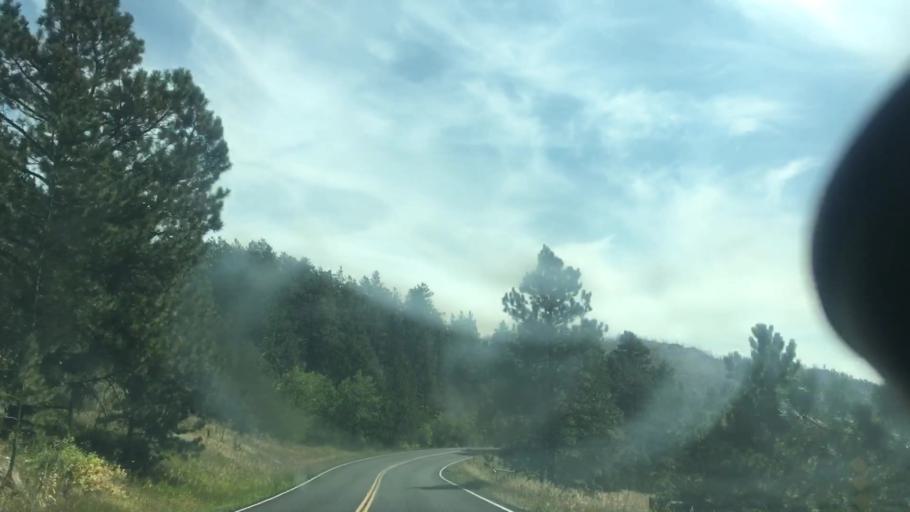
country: US
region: Colorado
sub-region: Larimer County
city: Laporte
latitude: 40.6053
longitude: -105.3462
